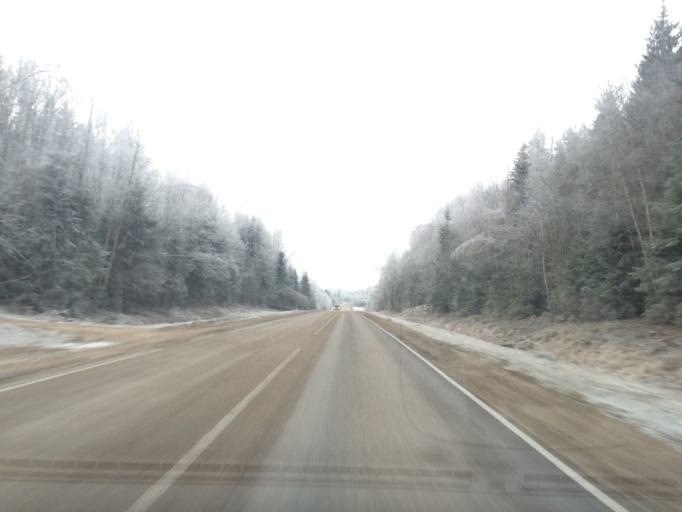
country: LV
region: Rezekne
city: Rezekne
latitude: 56.5965
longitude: 27.4186
